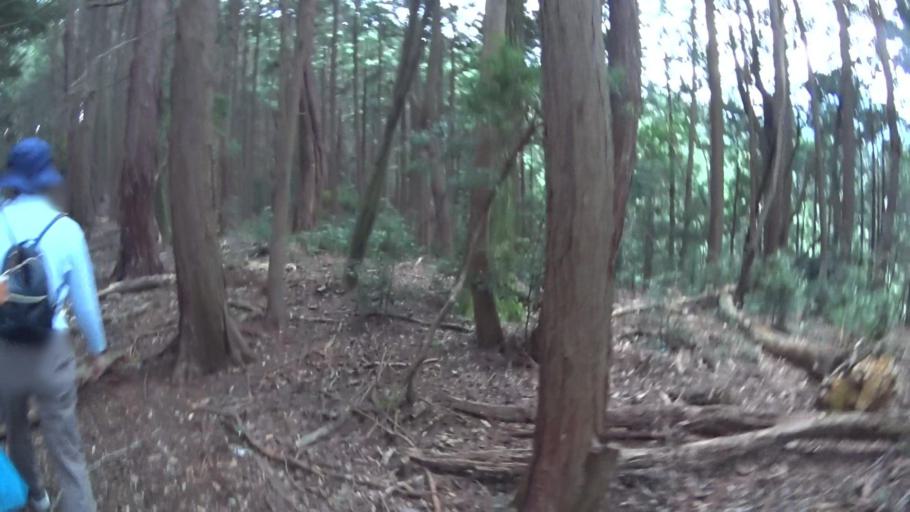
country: JP
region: Osaka
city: Kishiwada
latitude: 34.4959
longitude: 135.3285
